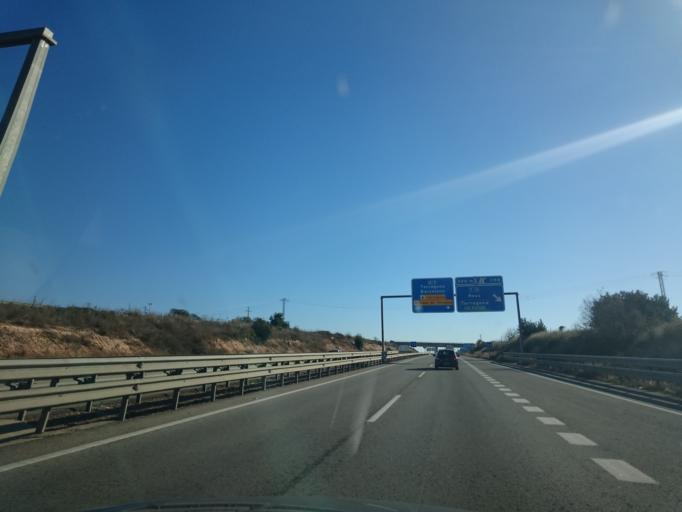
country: ES
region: Catalonia
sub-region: Provincia de Tarragona
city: Vila-seca
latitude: 41.1277
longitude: 1.1845
